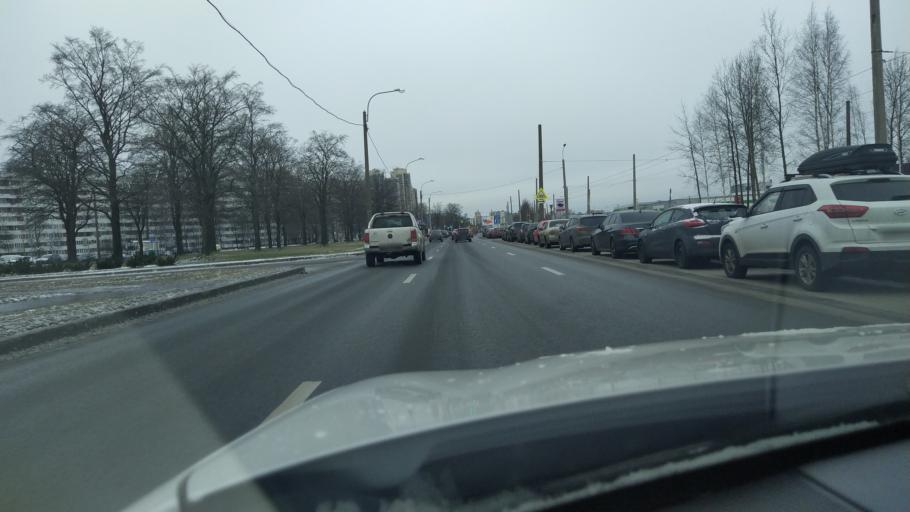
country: RU
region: St.-Petersburg
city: Grazhdanka
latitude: 60.0244
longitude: 30.4321
